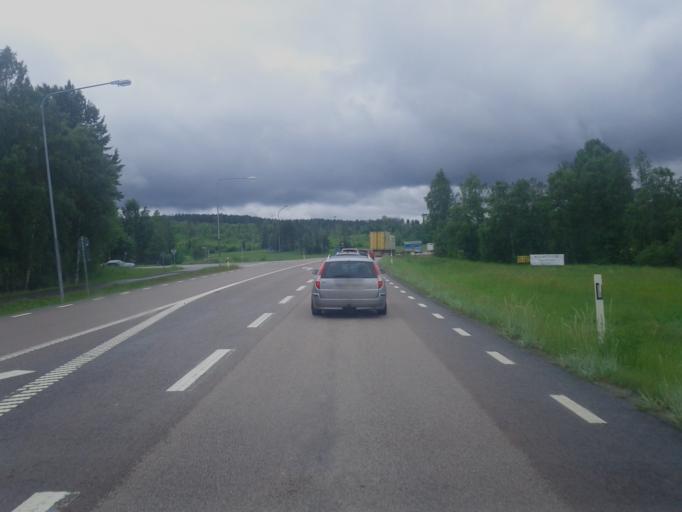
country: SE
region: Vaesternorrland
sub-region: Haernoesands Kommun
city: Haernoesand
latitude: 62.6661
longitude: 17.8464
